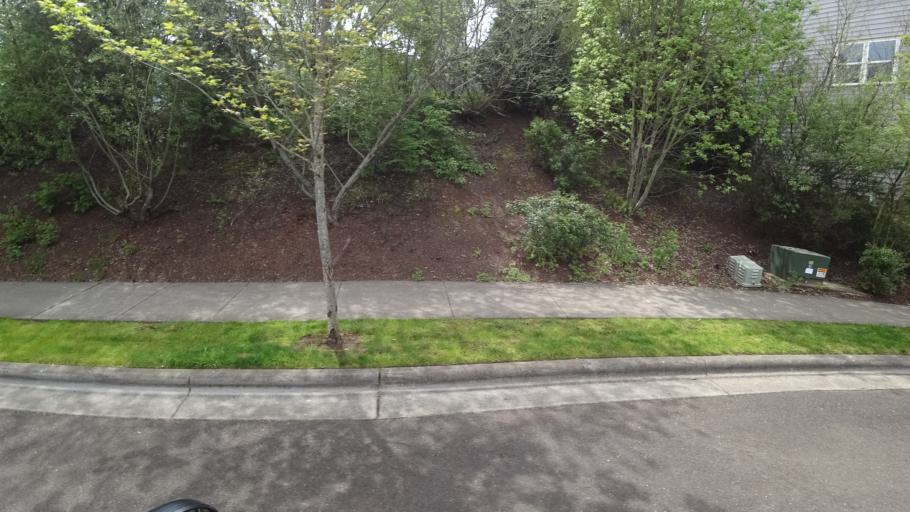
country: US
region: Oregon
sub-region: Washington County
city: Aloha
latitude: 45.4601
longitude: -122.8557
